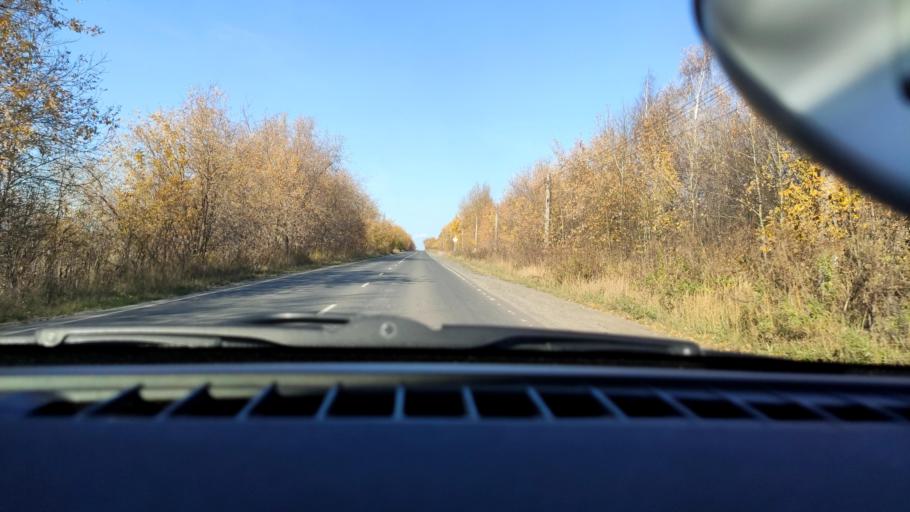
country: RU
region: Perm
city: Gamovo
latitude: 57.9010
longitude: 56.1765
